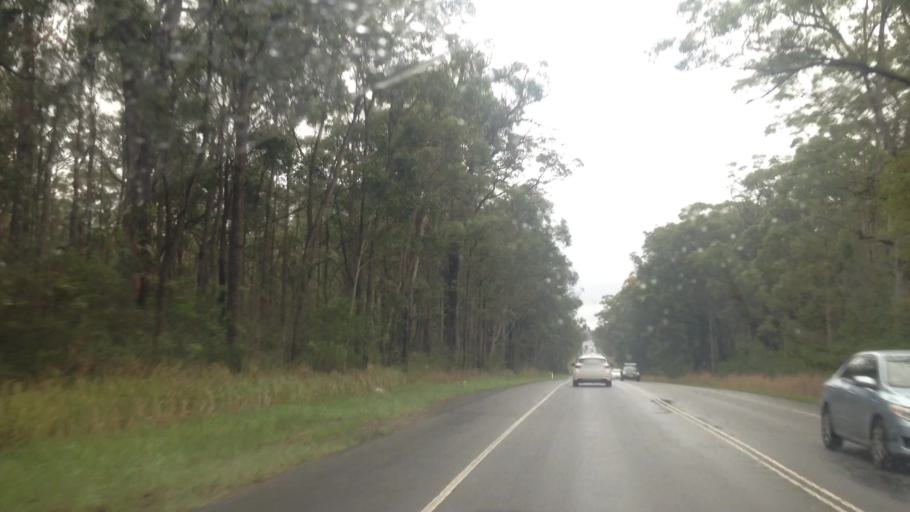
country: AU
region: New South Wales
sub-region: Lake Macquarie Shire
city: Dora Creek
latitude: -33.1380
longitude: 151.4774
